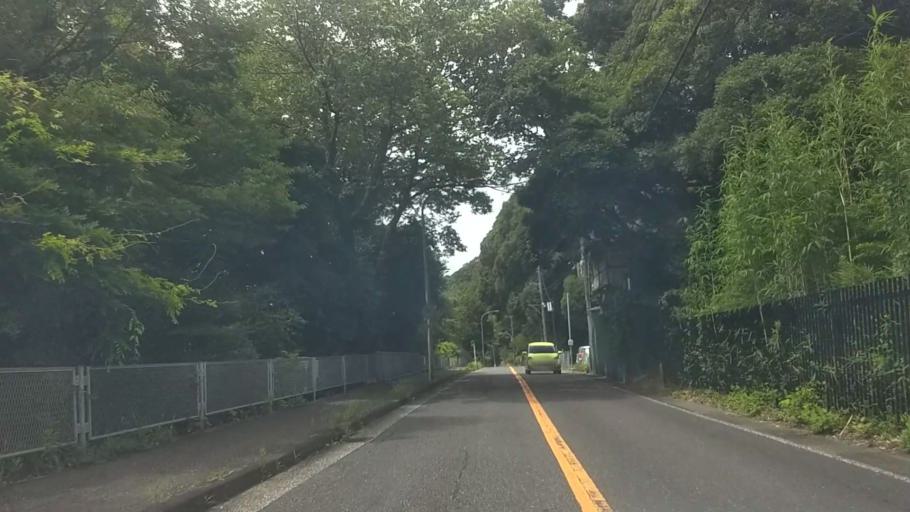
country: JP
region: Kanagawa
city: Yokosuka
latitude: 35.2590
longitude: 139.7179
